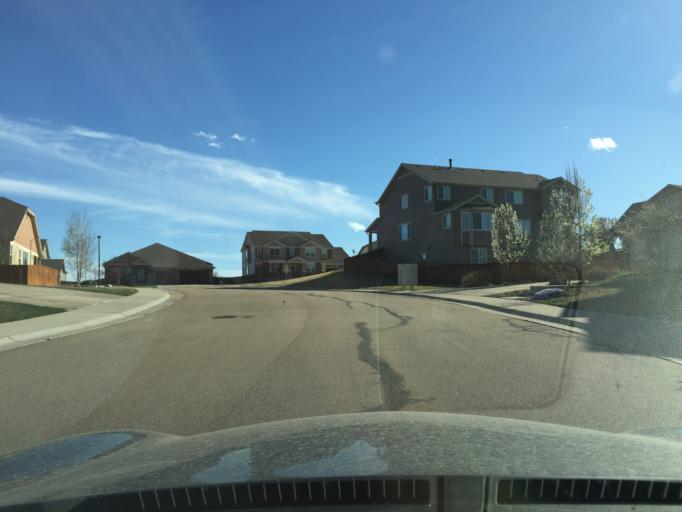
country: US
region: Colorado
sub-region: Boulder County
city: Erie
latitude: 40.0256
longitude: -105.0406
